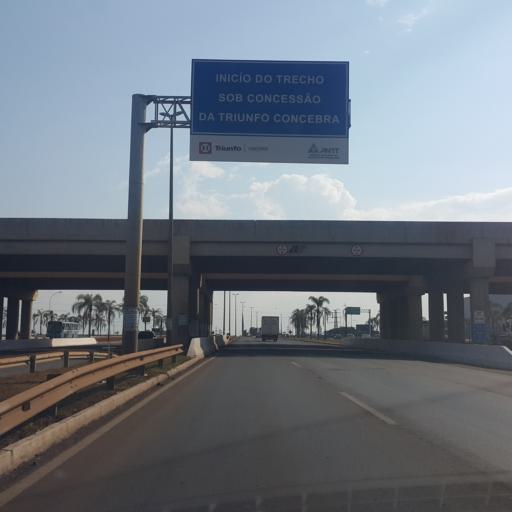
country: BR
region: Federal District
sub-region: Brasilia
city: Brasilia
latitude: -15.8822
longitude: -48.0598
